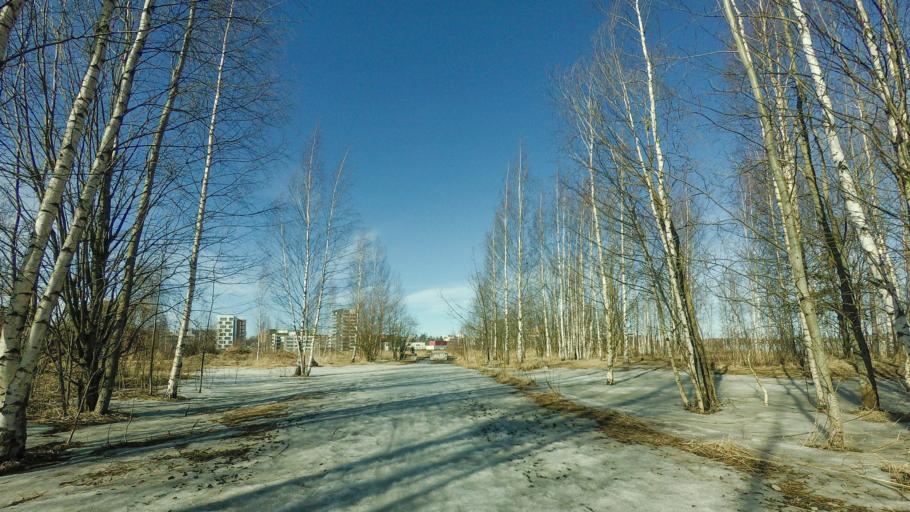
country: FI
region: Uusimaa
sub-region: Helsinki
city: Helsinki
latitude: 60.2008
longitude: 24.9784
